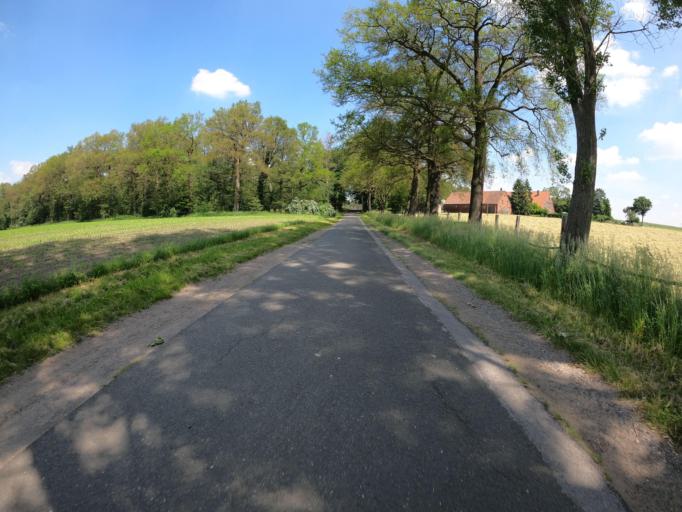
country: DE
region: North Rhine-Westphalia
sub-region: Regierungsbezirk Dusseldorf
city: Hunxe
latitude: 51.7097
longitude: 6.7129
